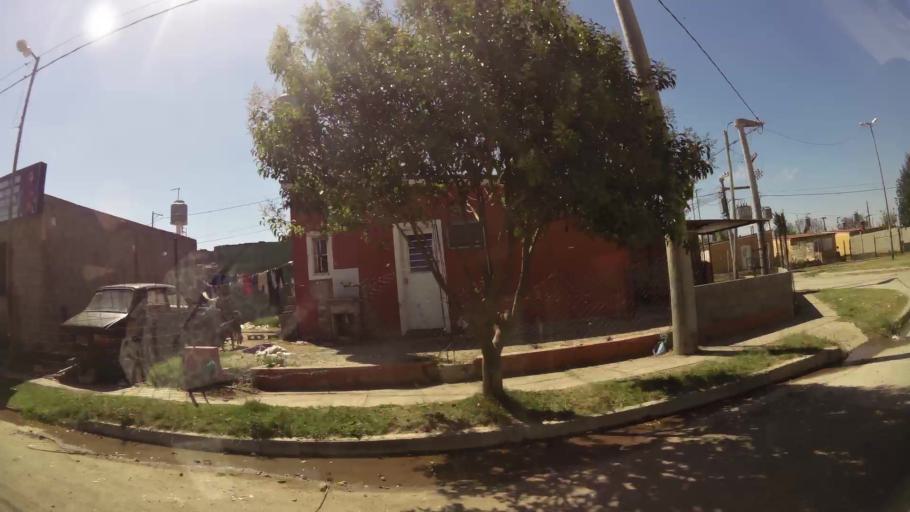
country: AR
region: Cordoba
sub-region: Departamento de Capital
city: Cordoba
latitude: -31.3705
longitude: -64.1630
